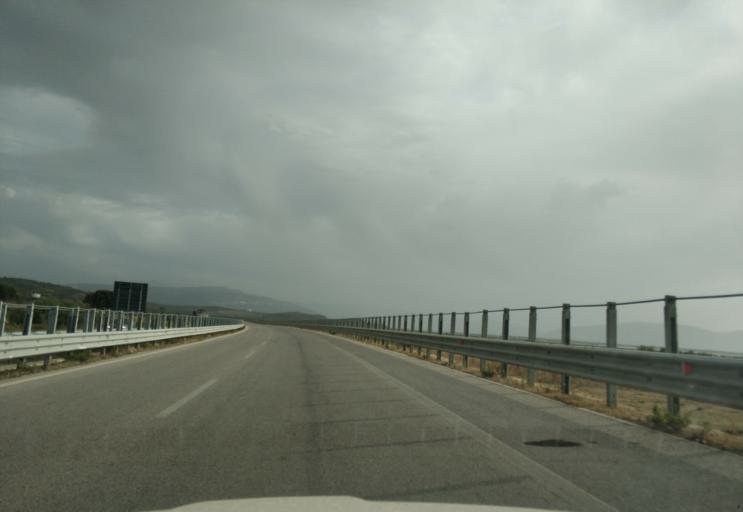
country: AL
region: Vlore
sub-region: Rrethi i Vlores
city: Novosele
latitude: 40.5460
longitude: 19.4599
